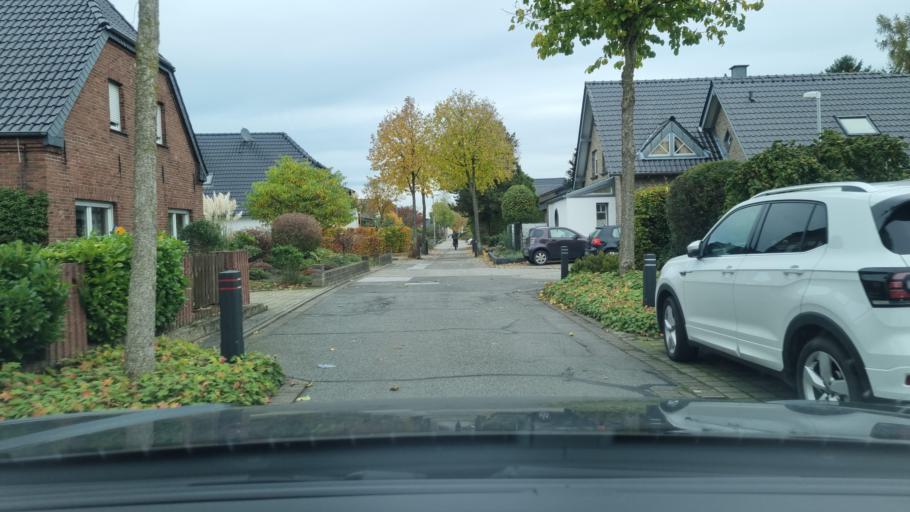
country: DE
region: North Rhine-Westphalia
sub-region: Regierungsbezirk Dusseldorf
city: Kranenburg
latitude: 51.7872
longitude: 6.0614
